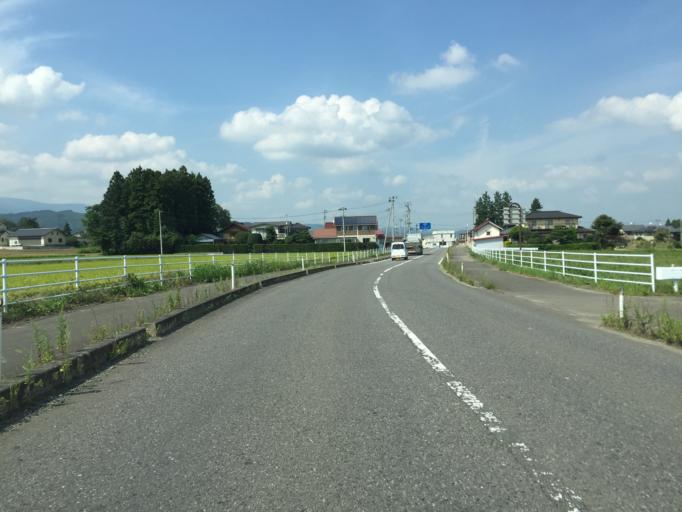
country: JP
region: Fukushima
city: Motomiya
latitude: 37.5427
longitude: 140.3840
